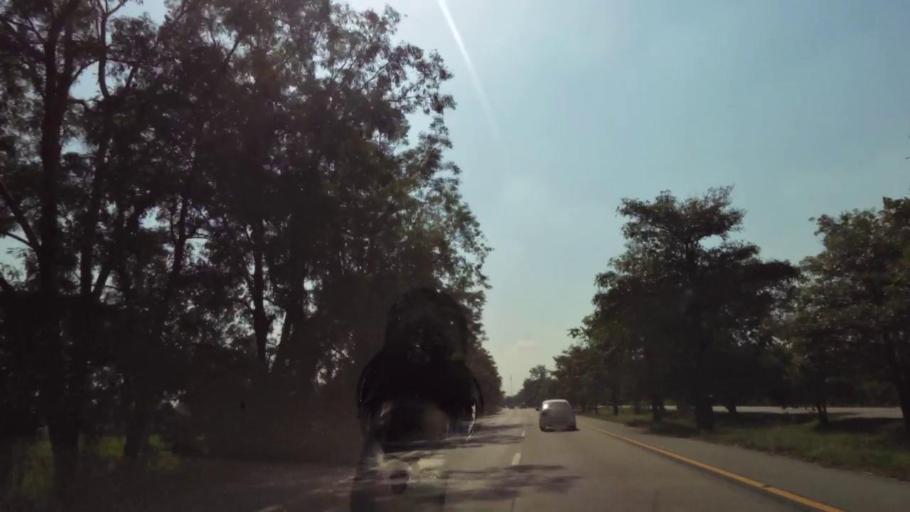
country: TH
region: Phitsanulok
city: Bang Rakam
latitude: 16.6452
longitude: 100.1502
